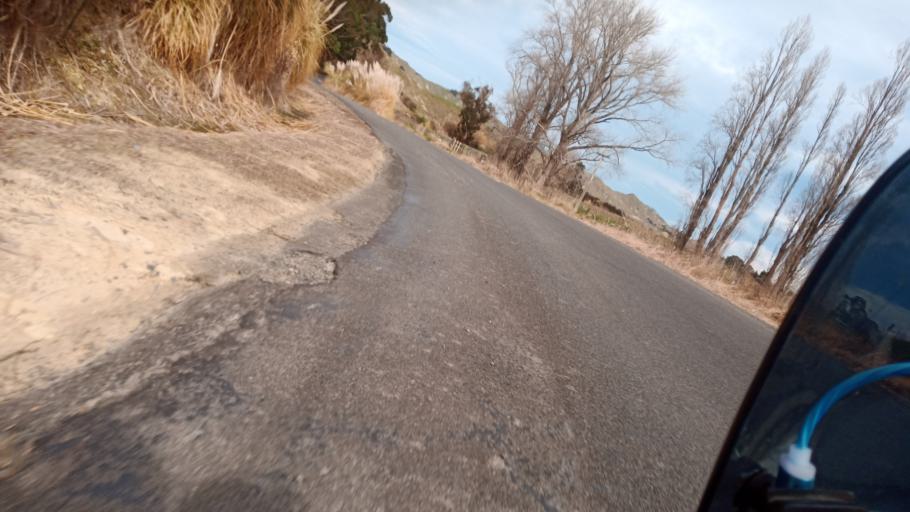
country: NZ
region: Hawke's Bay
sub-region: Wairoa District
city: Wairoa
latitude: -38.9679
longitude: 177.4368
